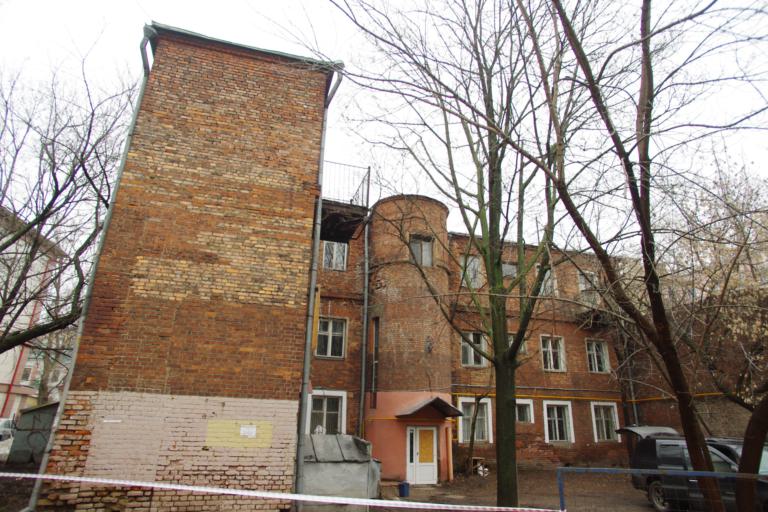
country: RU
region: Moskovskaya
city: Dorogomilovo
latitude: 55.7423
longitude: 37.5861
